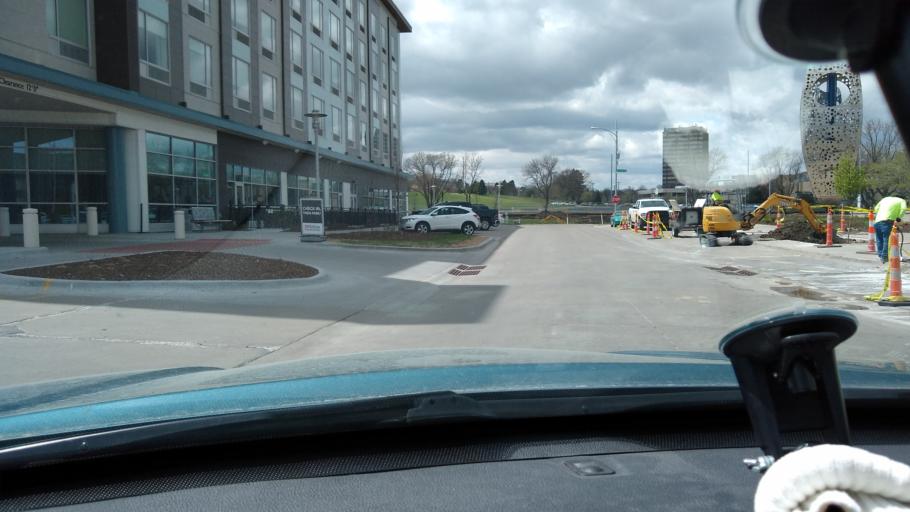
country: US
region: Nebraska
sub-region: Douglas County
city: Ralston
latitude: 41.2403
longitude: -96.0165
